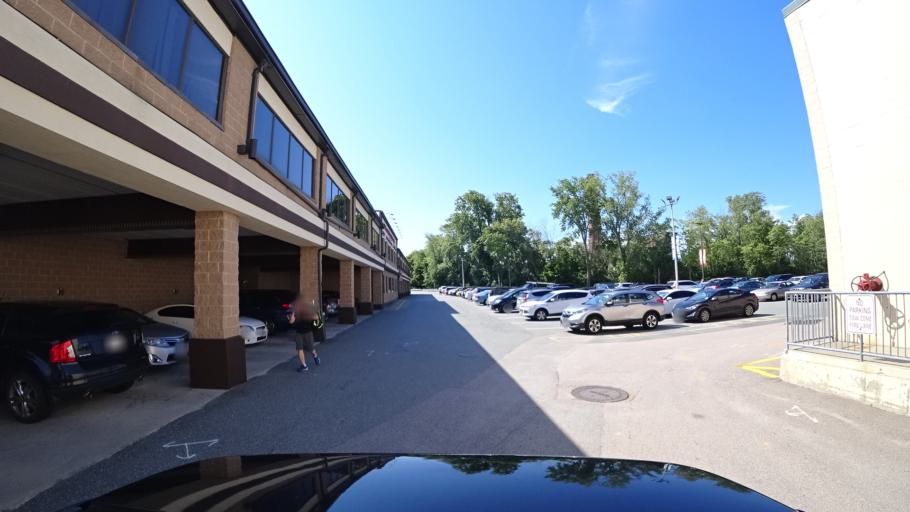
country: US
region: Massachusetts
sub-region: Norfolk County
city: Dedham
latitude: 42.2571
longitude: -71.1667
